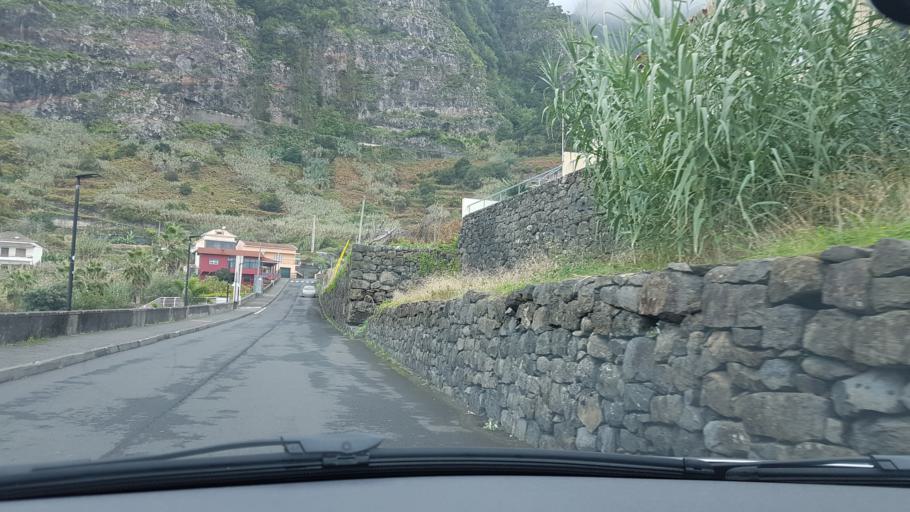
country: PT
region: Madeira
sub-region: Sao Vicente
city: Sao Vicente
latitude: 32.8281
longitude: -16.9855
